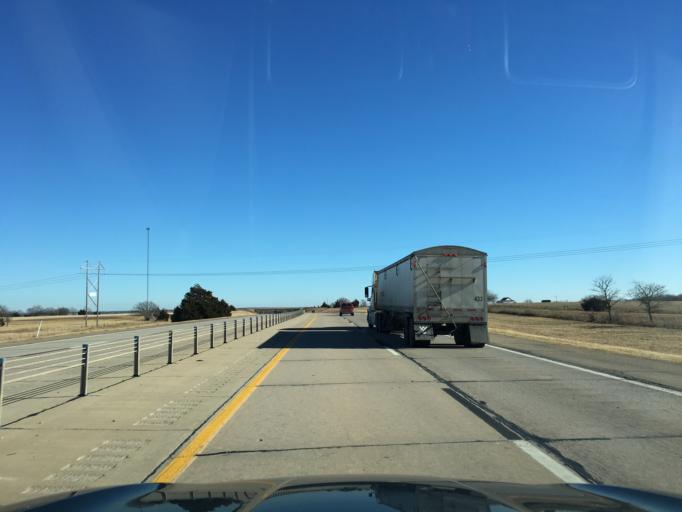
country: US
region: Oklahoma
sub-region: Pawnee County
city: Pawnee
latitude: 36.2253
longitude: -96.8969
